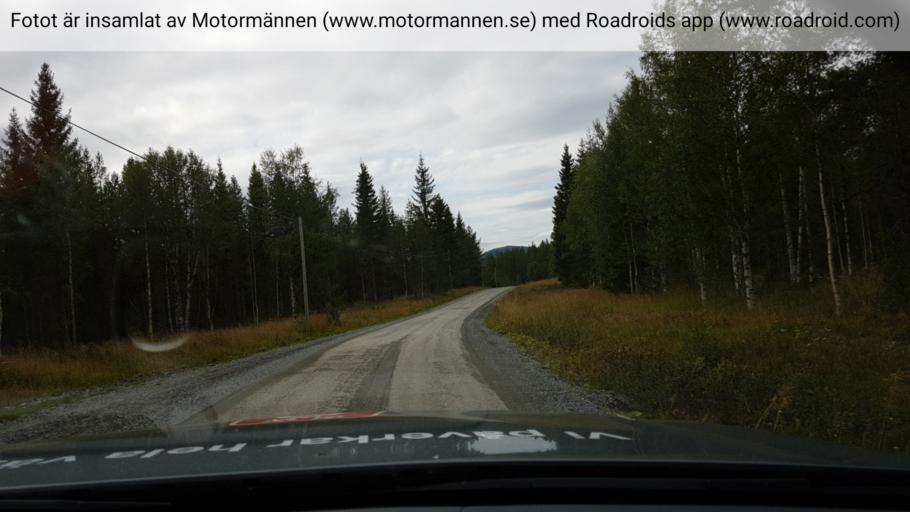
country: SE
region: Jaemtland
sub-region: Krokoms Kommun
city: Valla
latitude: 63.7064
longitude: 13.5778
